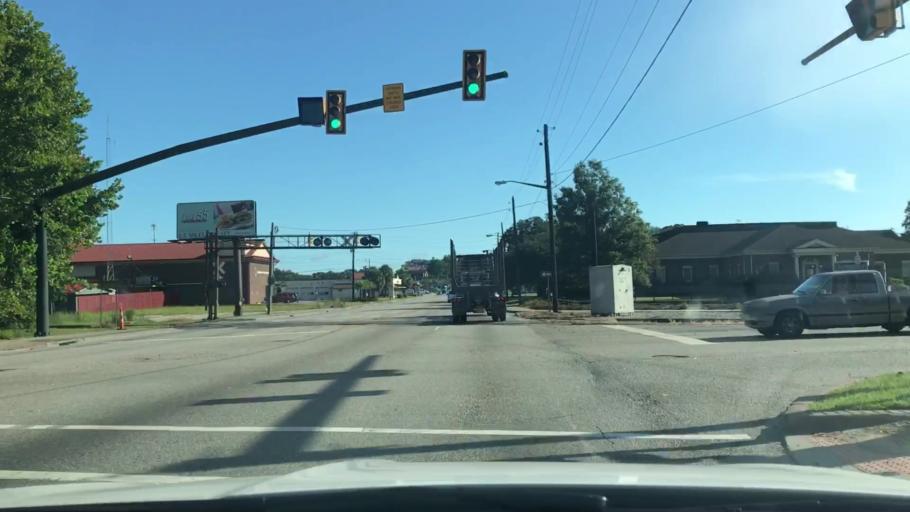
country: US
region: South Carolina
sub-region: Georgetown County
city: Georgetown
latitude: 33.3712
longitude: -79.2905
